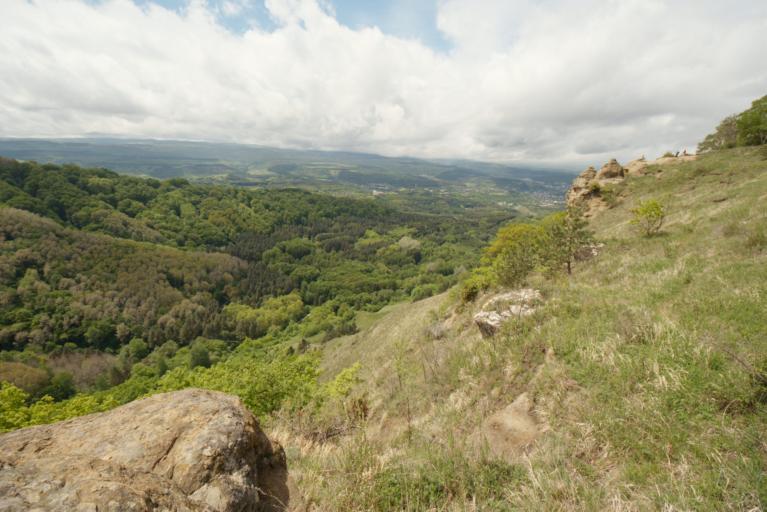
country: RU
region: Stavropol'skiy
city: Kislovodsk
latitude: 43.8957
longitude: 42.7606
